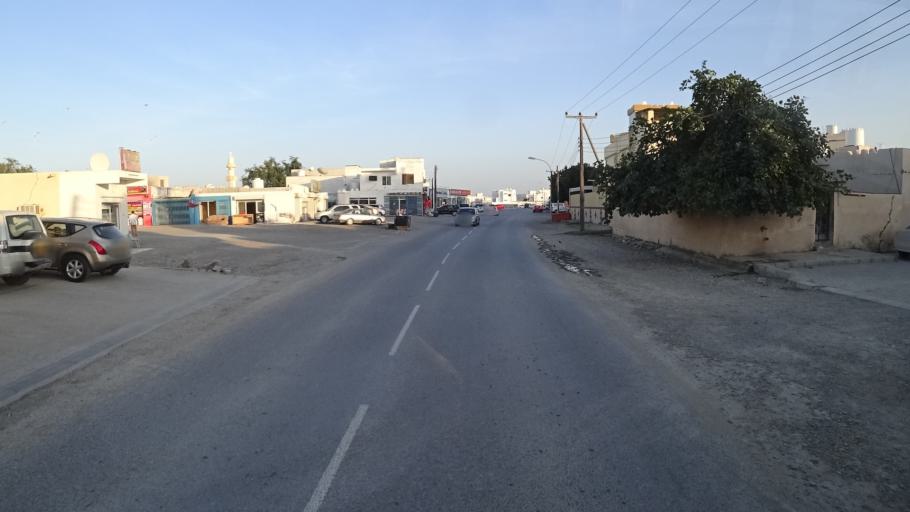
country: OM
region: Al Batinah
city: Barka'
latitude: 23.7066
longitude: 57.8986
